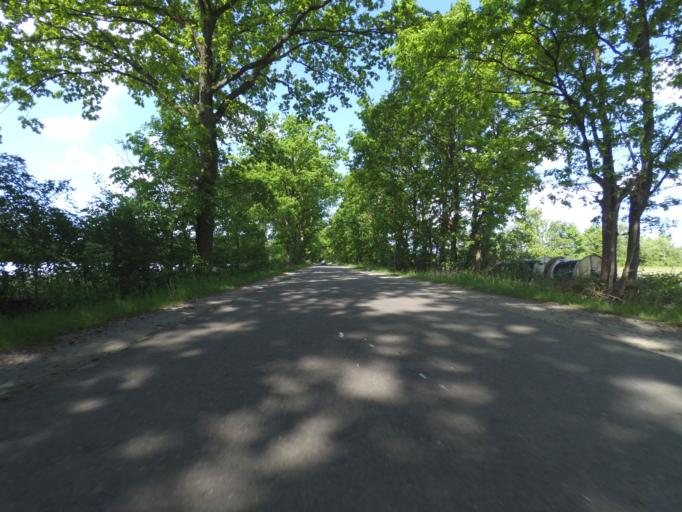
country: DE
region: Lower Saxony
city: Wathlingen
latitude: 52.5338
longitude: 10.1285
